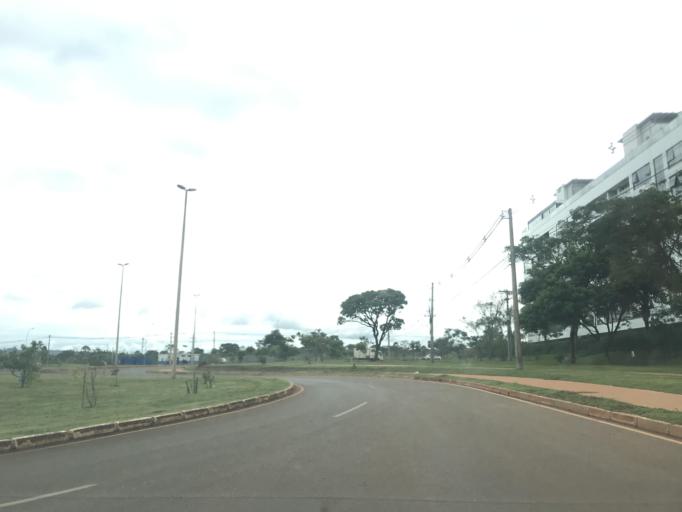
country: BR
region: Federal District
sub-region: Brasilia
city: Brasilia
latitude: -15.7401
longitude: -47.9109
